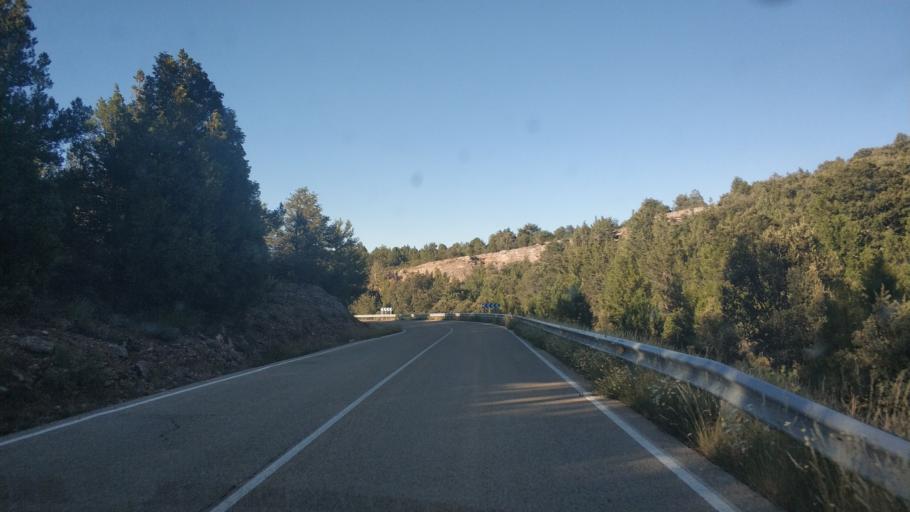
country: ES
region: Castille and Leon
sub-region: Provincia de Soria
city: Montejo de Tiermes
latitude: 41.4240
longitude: -3.2026
